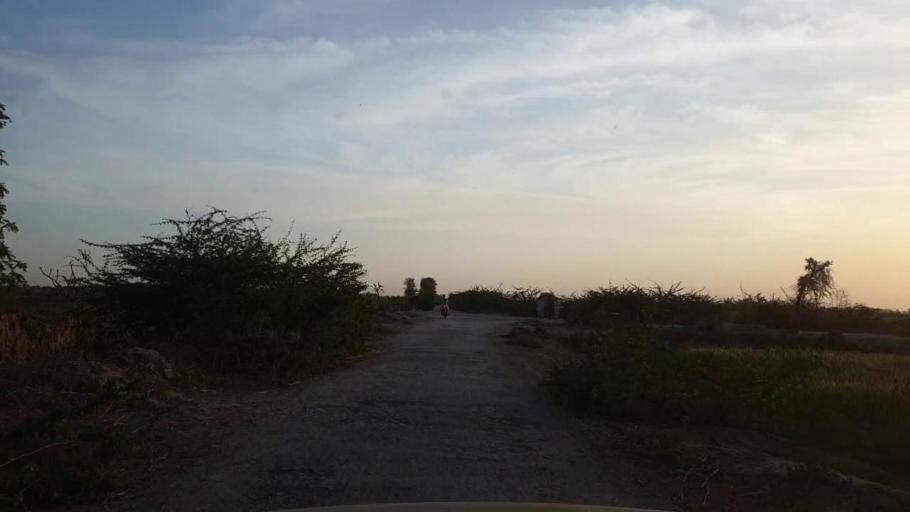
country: PK
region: Sindh
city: Kunri
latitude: 25.1243
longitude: 69.5695
